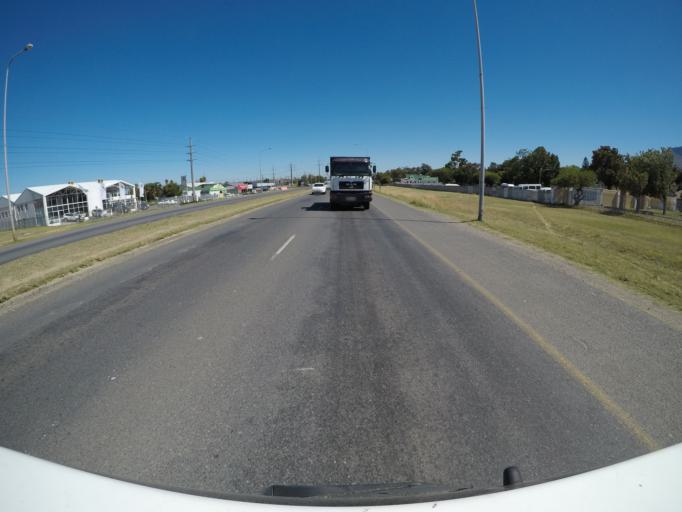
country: ZA
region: Western Cape
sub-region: Cape Winelands District Municipality
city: Stellenbosch
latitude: -34.0927
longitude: 18.8432
